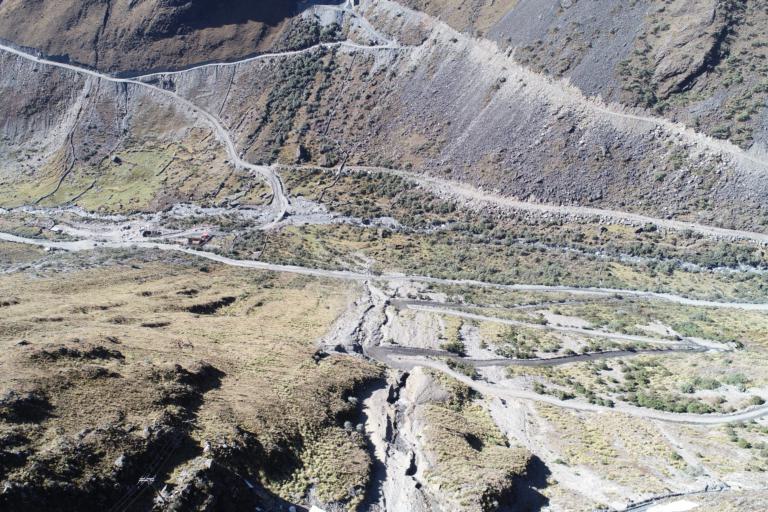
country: BO
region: La Paz
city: Sorata
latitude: -15.6540
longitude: -68.5350
